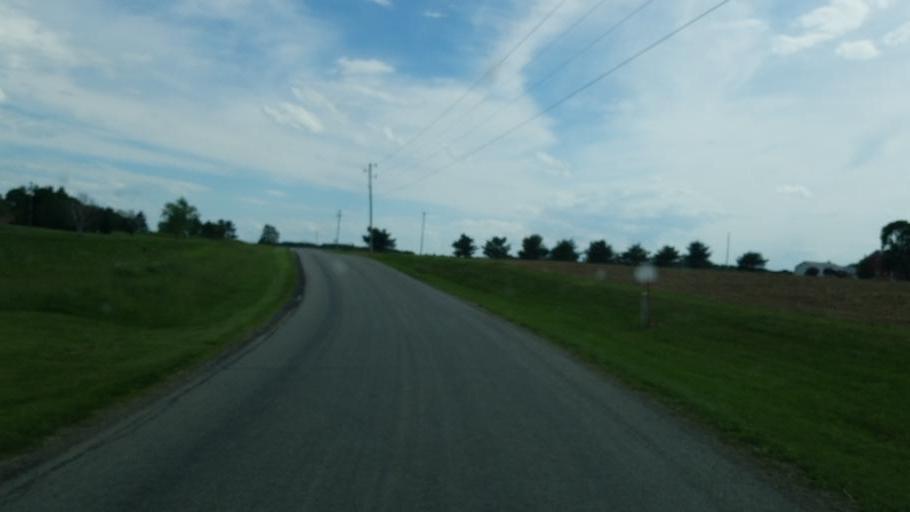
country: US
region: Ohio
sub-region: Huron County
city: Greenwich
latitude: 40.9014
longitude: -82.5326
